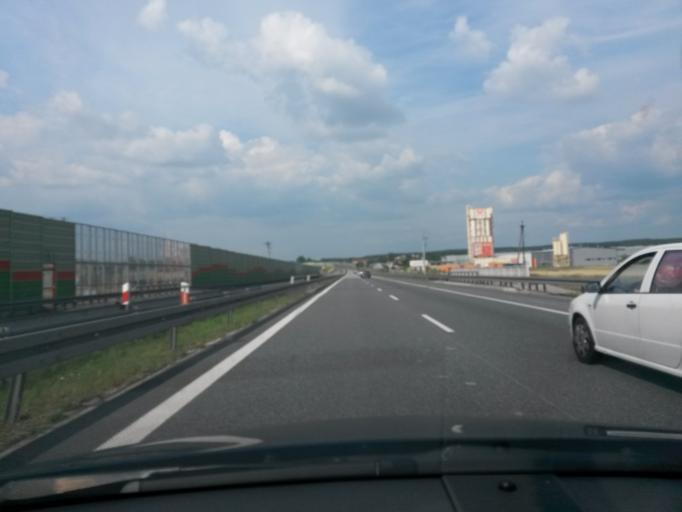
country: PL
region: Lodz Voivodeship
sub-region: Powiat rawski
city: Rawa Mazowiecka
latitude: 51.7598
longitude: 20.2624
